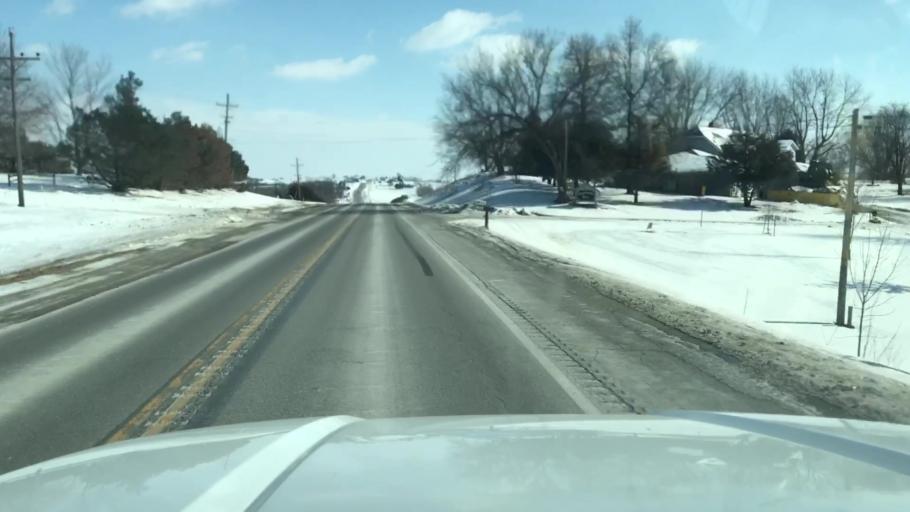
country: US
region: Missouri
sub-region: Nodaway County
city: Maryville
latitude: 40.3445
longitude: -94.7911
